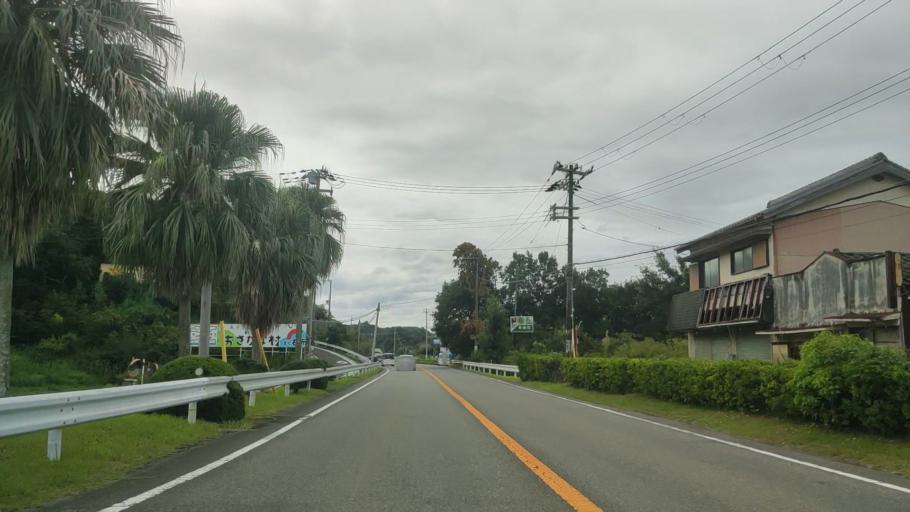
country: JP
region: Wakayama
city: Tanabe
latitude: 33.6982
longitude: 135.3884
